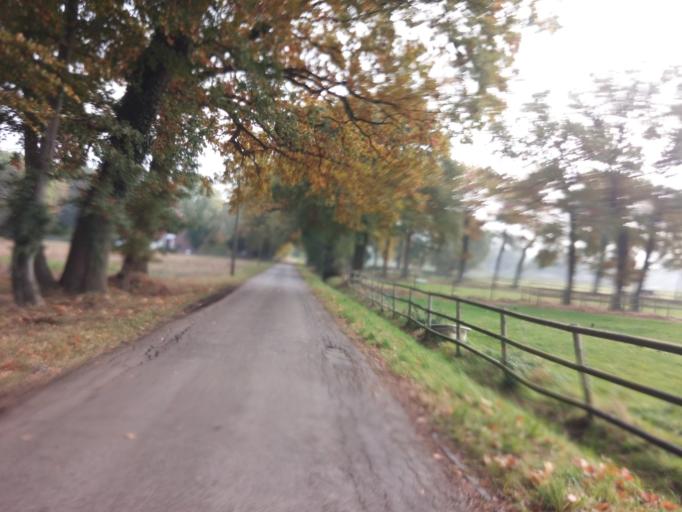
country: DE
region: North Rhine-Westphalia
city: Dorsten
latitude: 51.6234
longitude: 7.0056
